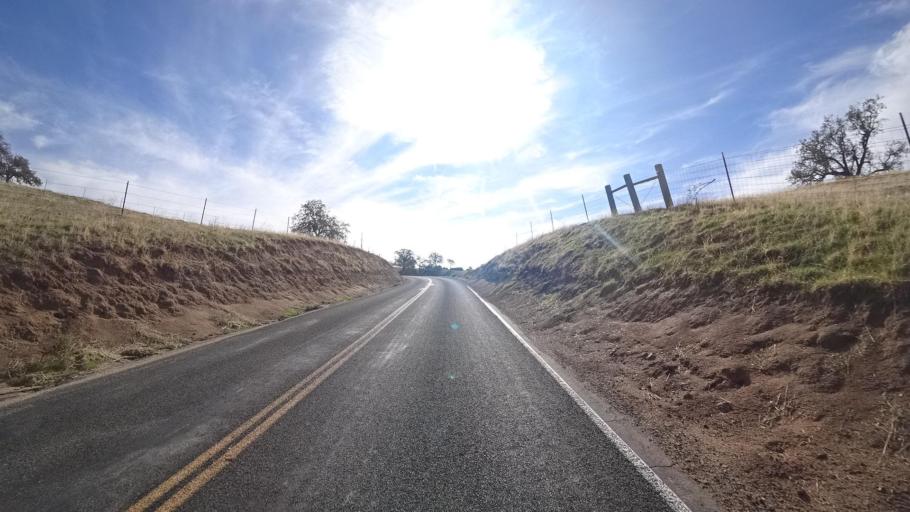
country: US
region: California
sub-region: Kern County
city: Oildale
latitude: 35.6192
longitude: -118.8542
